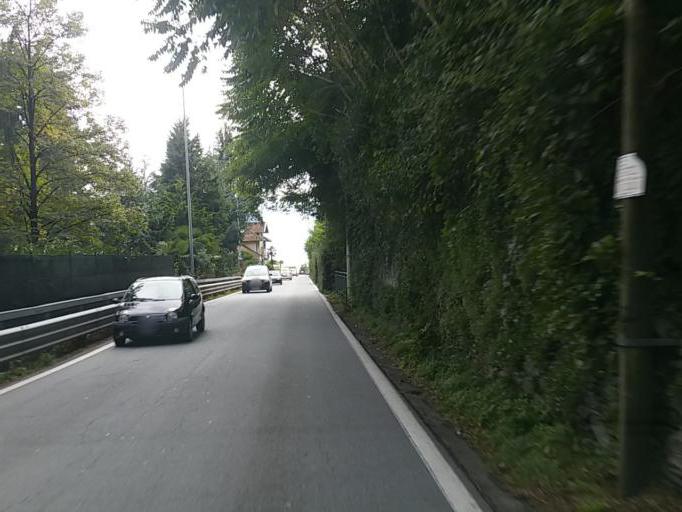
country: IT
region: Piedmont
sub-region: Provincia Verbano-Cusio-Ossola
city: Cannero Riviera
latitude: 46.0180
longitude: 8.6718
